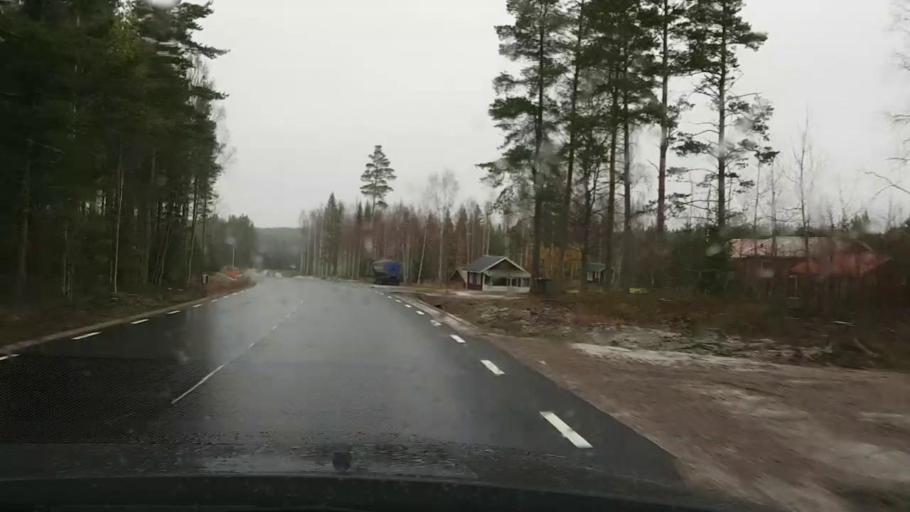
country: SE
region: Vaestra Goetaland
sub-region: Karlsborgs Kommun
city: Karlsborg
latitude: 58.7088
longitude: 14.5046
